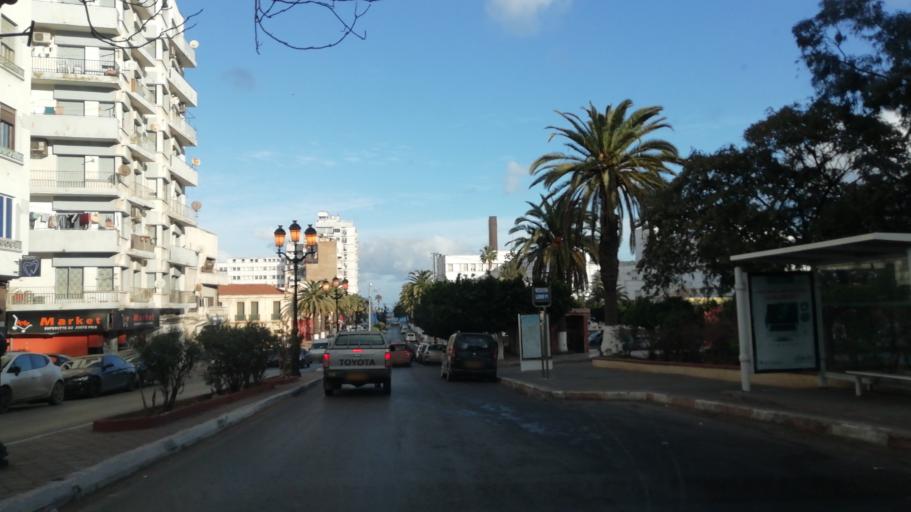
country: DZ
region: Oran
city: Oran
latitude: 35.7042
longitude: -0.6312
